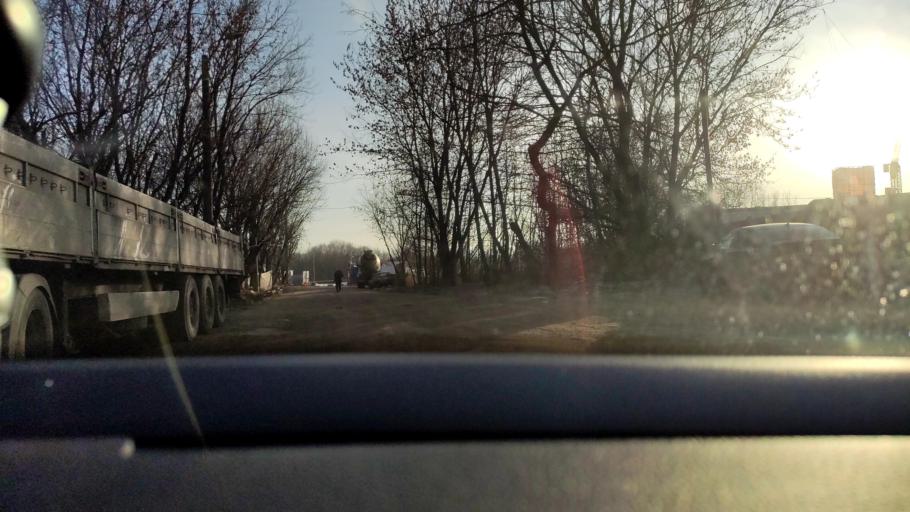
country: RU
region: Moskovskaya
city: Fili
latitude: 55.7503
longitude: 37.4592
